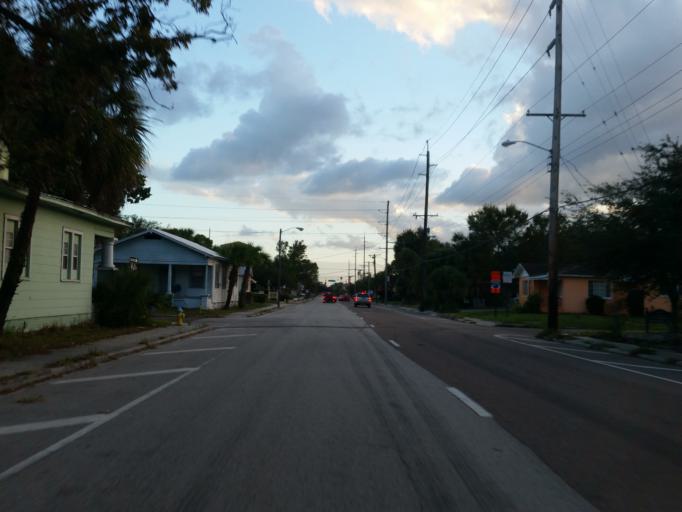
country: US
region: Florida
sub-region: Hillsborough County
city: Tampa
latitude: 27.9540
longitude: -82.4850
